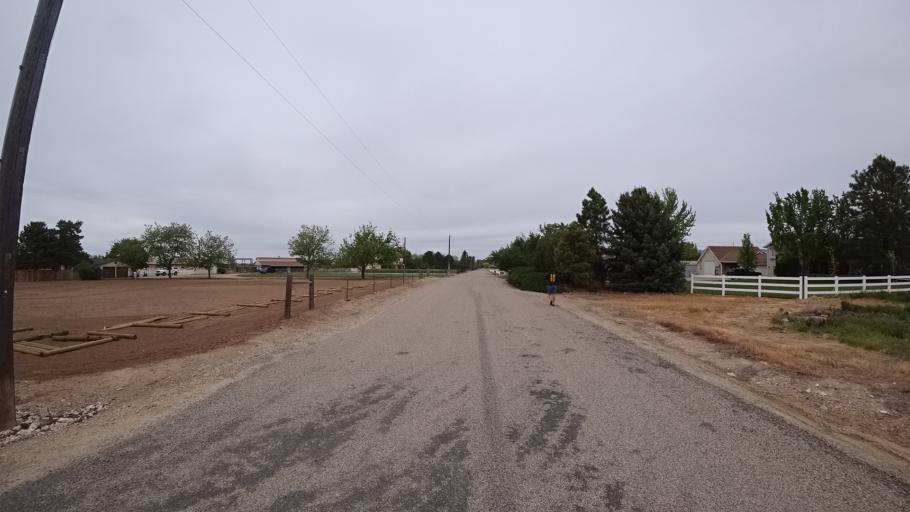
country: US
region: Idaho
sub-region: Ada County
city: Kuna
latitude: 43.4981
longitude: -116.3394
